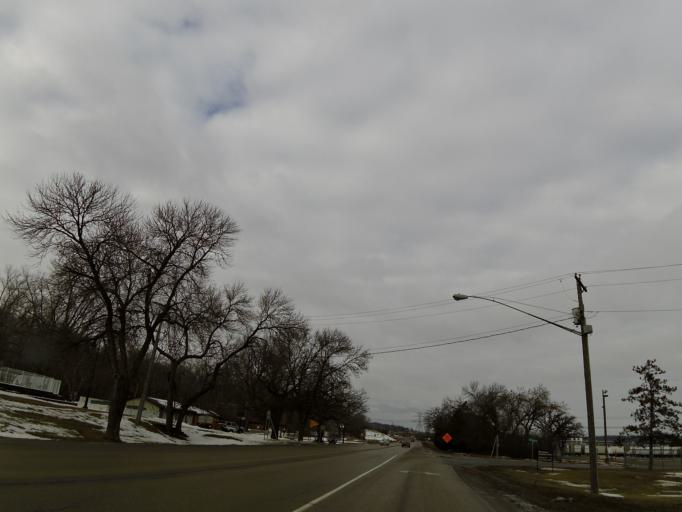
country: US
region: Minnesota
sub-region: Washington County
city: Bayport
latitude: 45.0250
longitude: -92.7824
